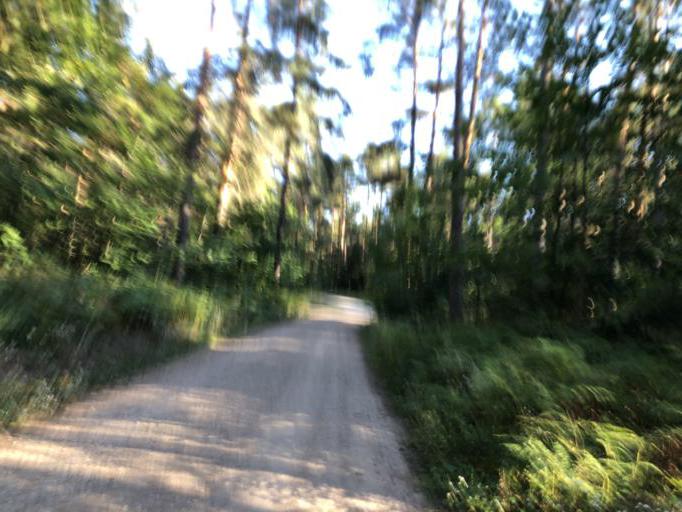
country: DE
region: Bavaria
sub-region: Regierungsbezirk Mittelfranken
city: Uttenreuth
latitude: 49.5551
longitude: 11.0784
